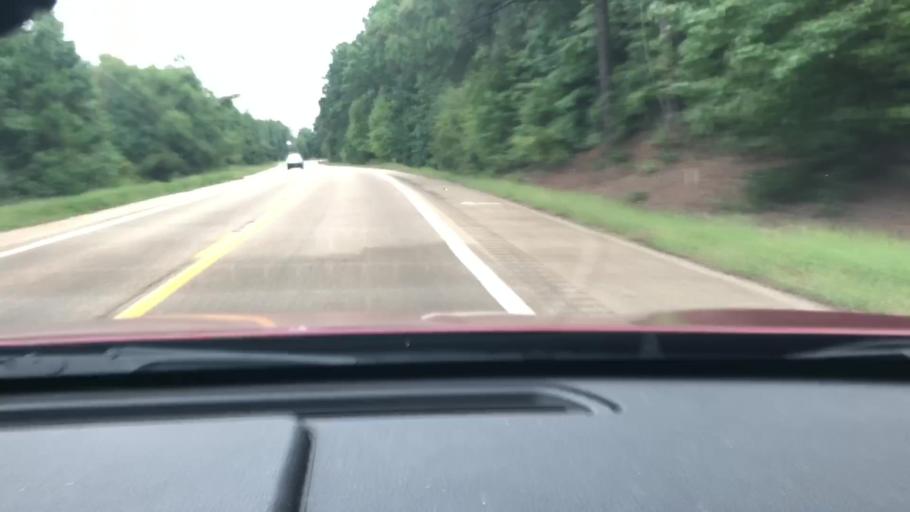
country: US
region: Arkansas
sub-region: Miller County
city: Texarkana
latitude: 33.4193
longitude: -93.8311
